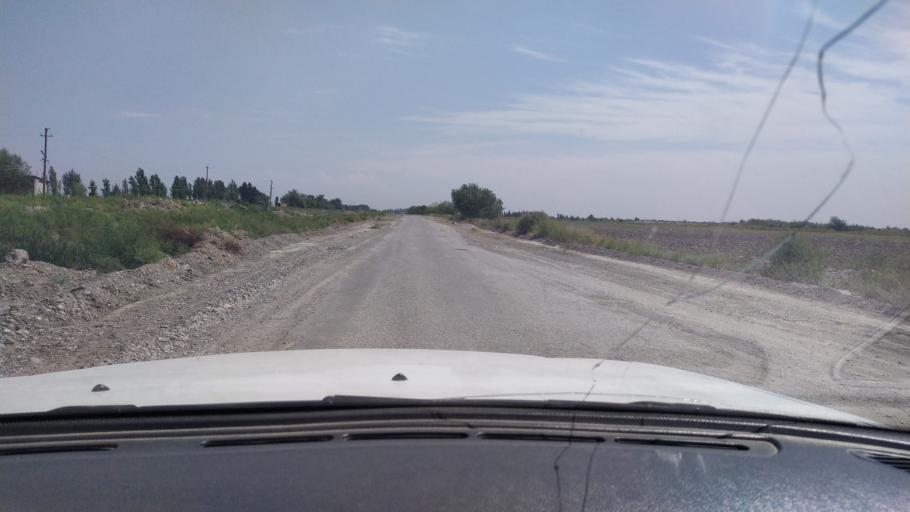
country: UZ
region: Namangan
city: Toshbuloq
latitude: 40.7932
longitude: 71.5755
